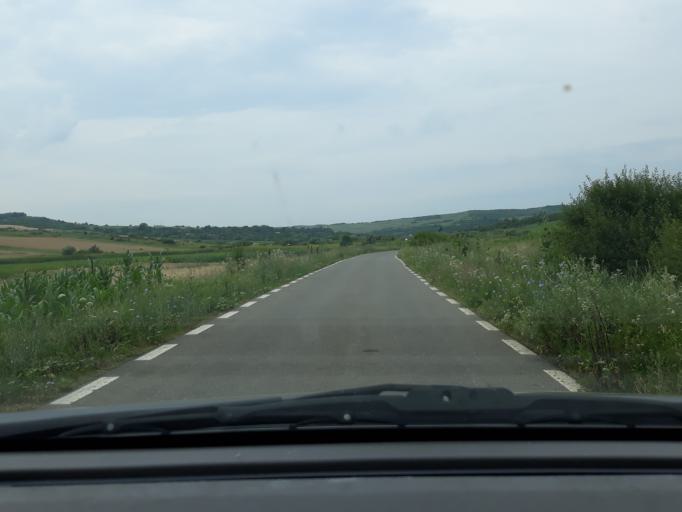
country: RO
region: Salaj
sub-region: Comuna Criseni
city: Criseni
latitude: 47.2711
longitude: 23.0701
